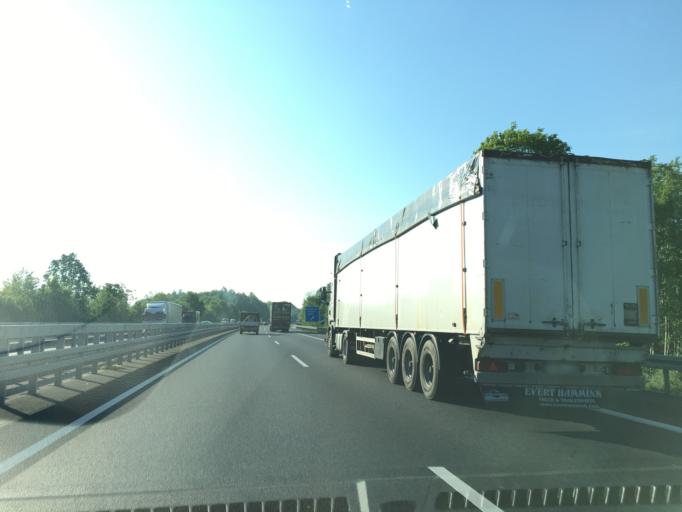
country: DE
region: Lower Saxony
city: Osnabrueck
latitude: 52.2644
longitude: 8.0021
